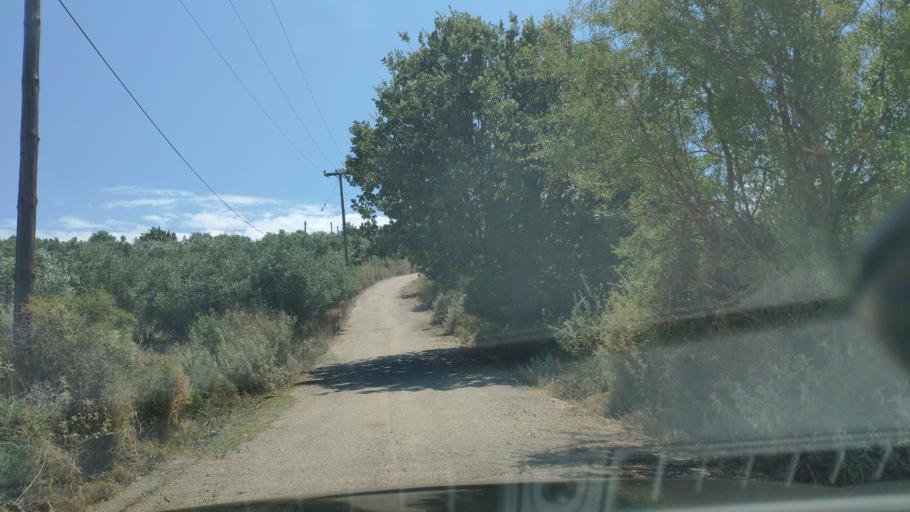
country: GR
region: West Greece
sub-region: Nomos Aitolias kai Akarnanias
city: Amfilochia
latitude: 38.9008
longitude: 21.0958
